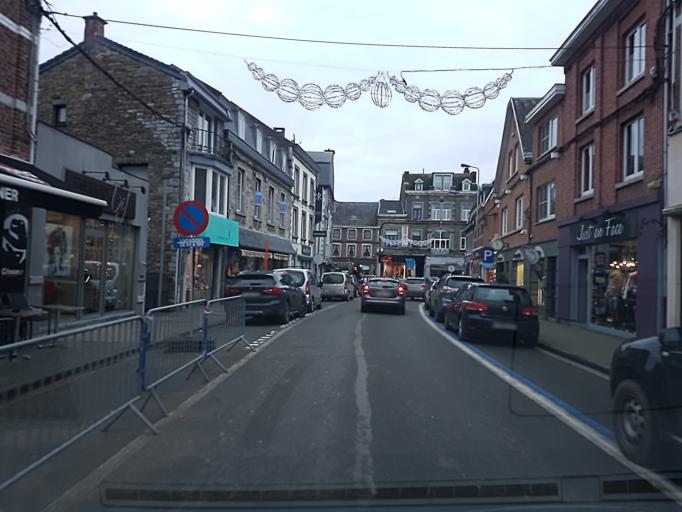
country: BE
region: Wallonia
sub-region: Province de Liege
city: Aywaille
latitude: 50.4746
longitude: 5.6744
